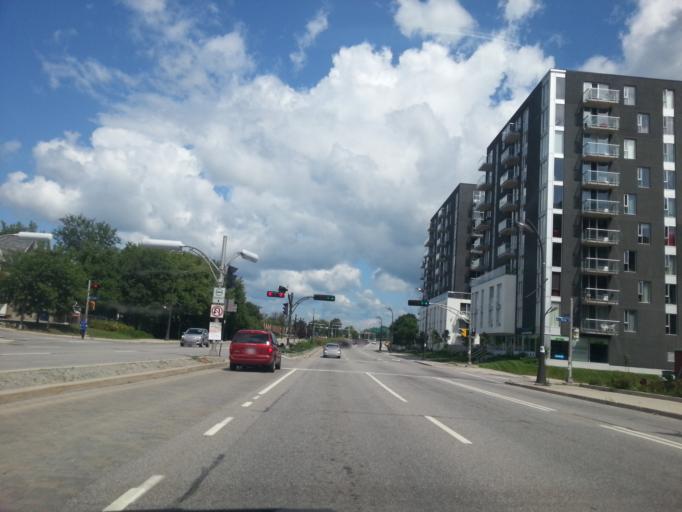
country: CA
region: Ontario
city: Ottawa
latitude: 45.4345
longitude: -75.7124
